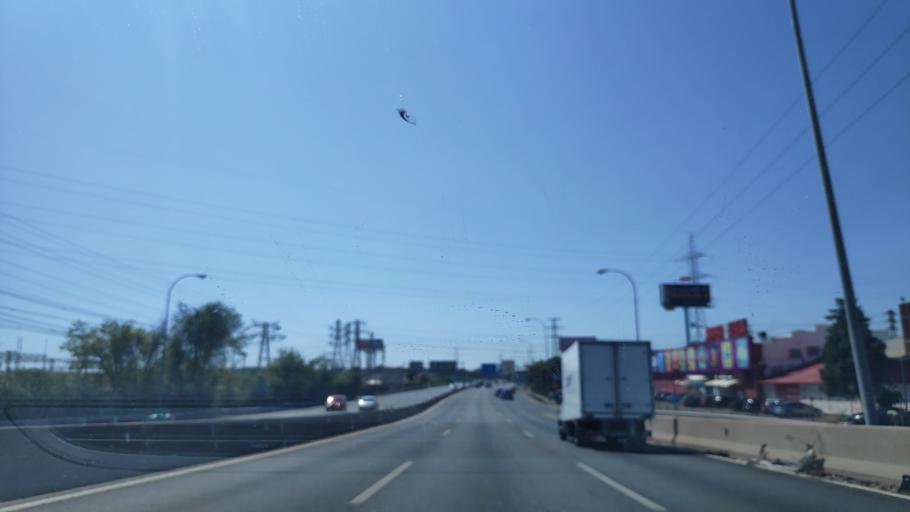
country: ES
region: Madrid
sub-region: Provincia de Madrid
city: Villaverde
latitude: 40.3368
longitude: -3.7246
